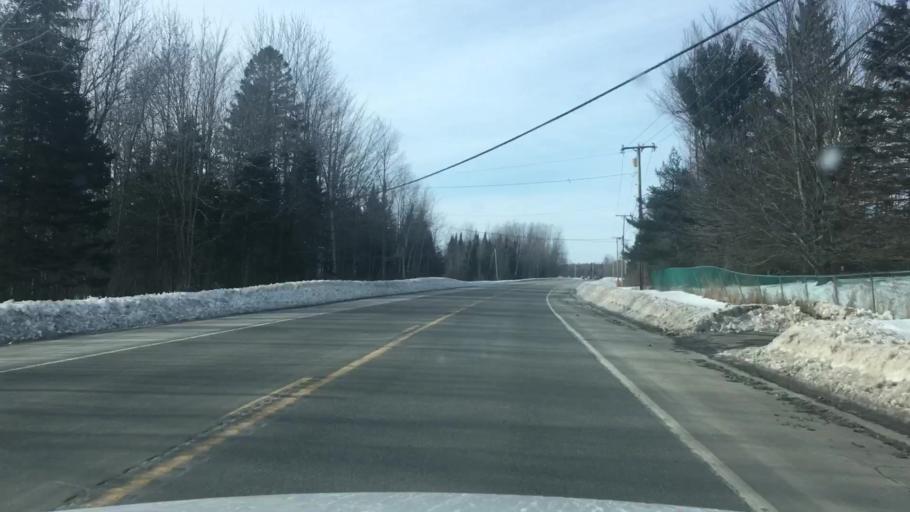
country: US
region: Maine
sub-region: Penobscot County
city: Kenduskeag
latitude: 44.9069
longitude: -68.8933
